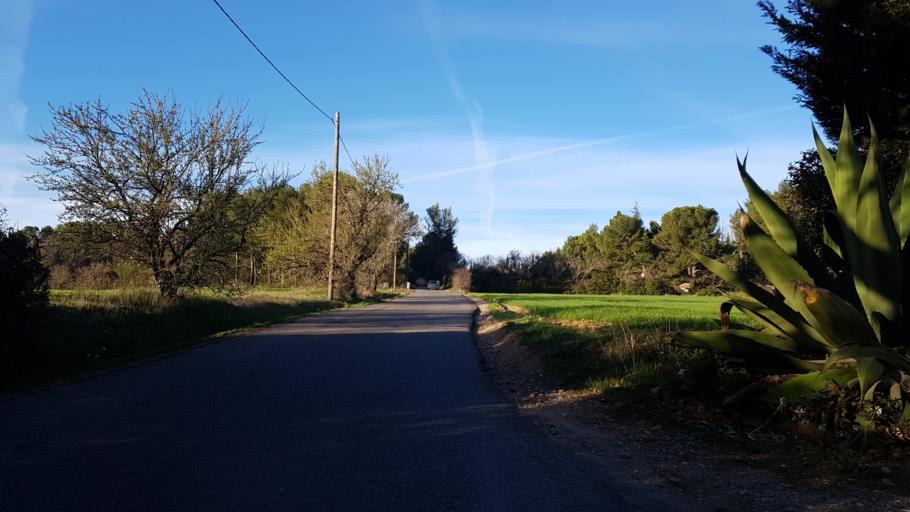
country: FR
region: Provence-Alpes-Cote d'Azur
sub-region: Departement des Bouches-du-Rhone
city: Bouc-Bel-Air
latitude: 43.4981
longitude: 5.3978
